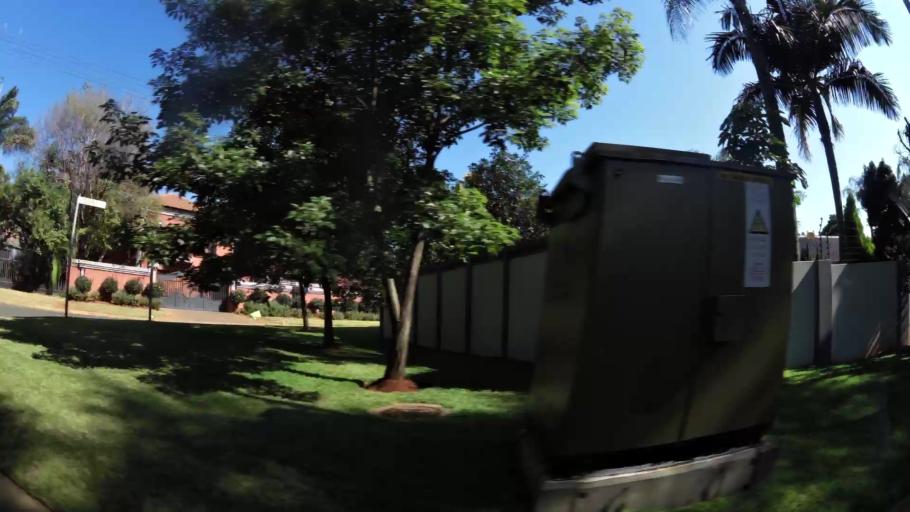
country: ZA
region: Gauteng
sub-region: City of Tshwane Metropolitan Municipality
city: Pretoria
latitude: -25.6876
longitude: 28.2252
